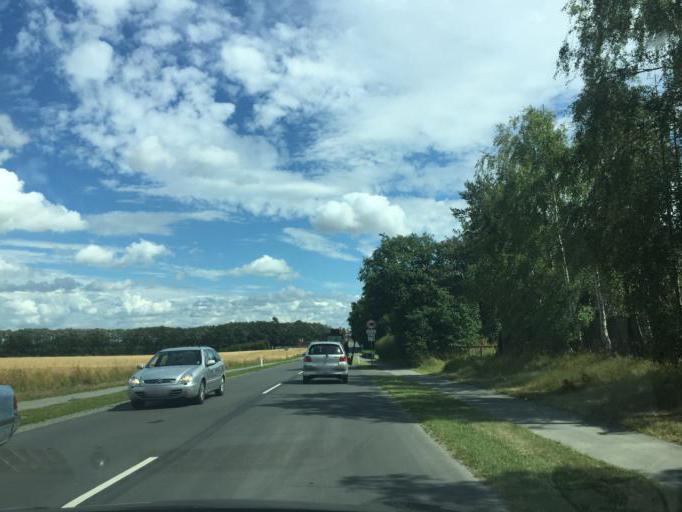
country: DK
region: South Denmark
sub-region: Nordfyns Kommune
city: Otterup
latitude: 55.5222
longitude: 10.3620
